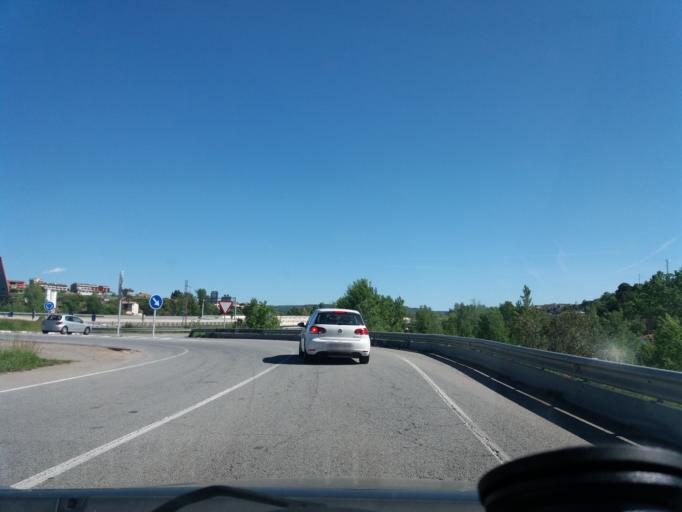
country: ES
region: Catalonia
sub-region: Provincia de Barcelona
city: Gironella
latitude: 42.0459
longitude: 1.8751
